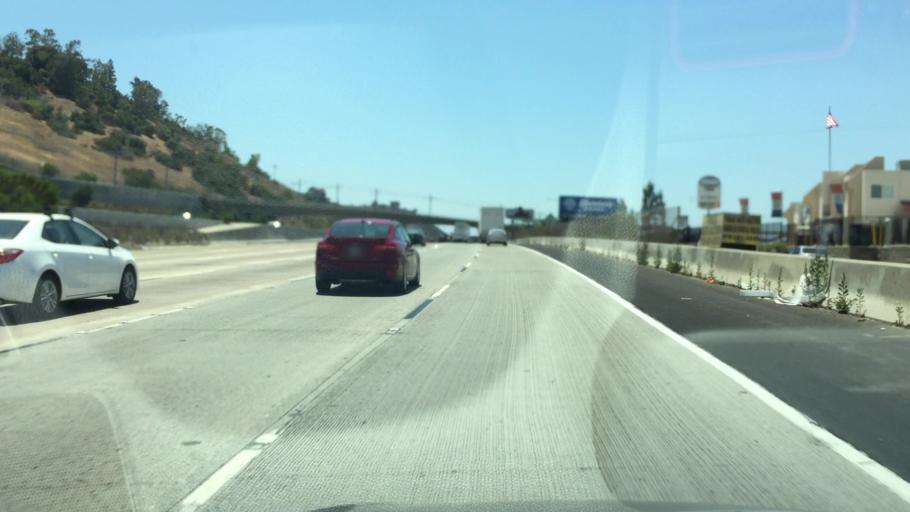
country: US
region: California
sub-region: San Diego County
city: La Mesa
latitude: 32.7808
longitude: -117.0926
